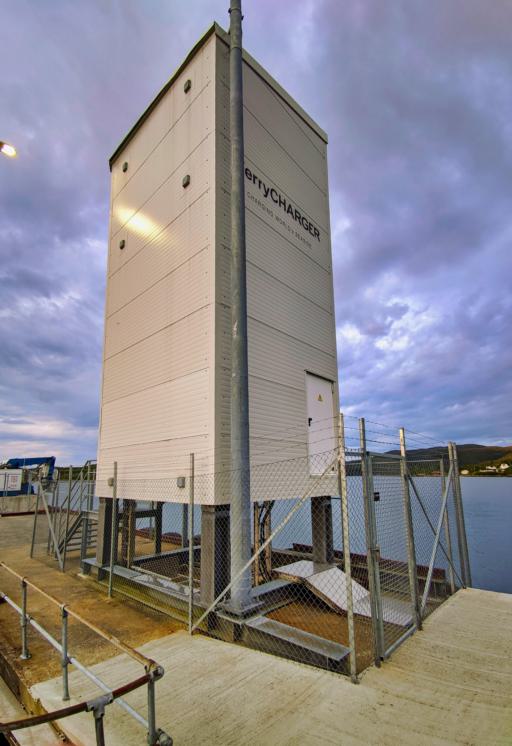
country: NO
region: Hordaland
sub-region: Tysnes
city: Uggdal
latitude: 60.0471
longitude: 5.5240
